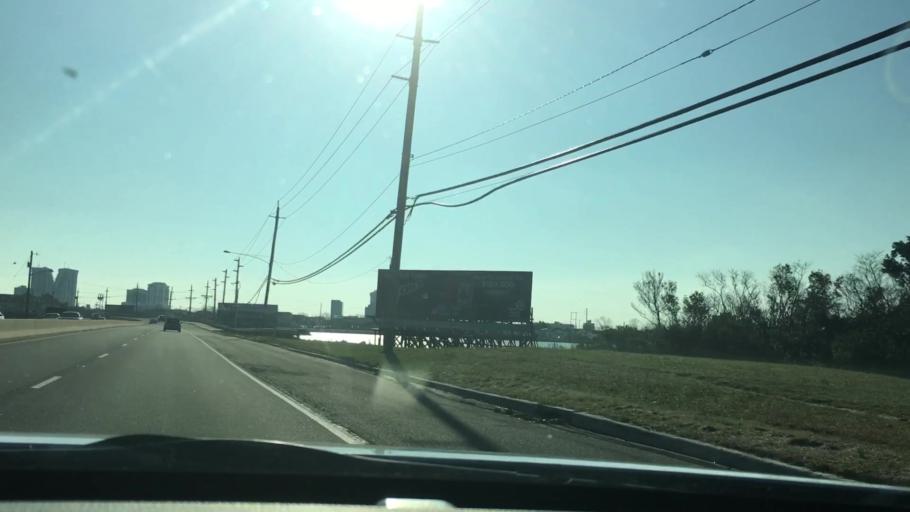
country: US
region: New Jersey
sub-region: Atlantic County
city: Ventnor City
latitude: 39.3633
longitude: -74.4677
